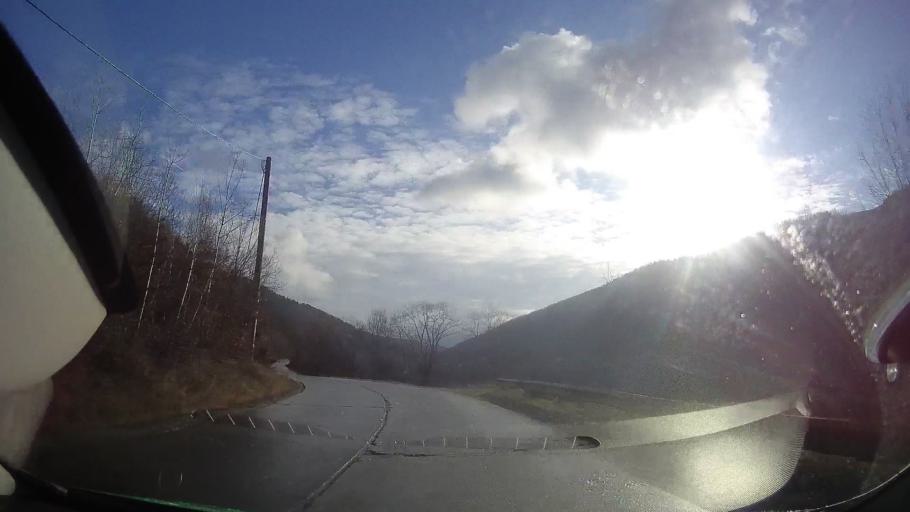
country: RO
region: Alba
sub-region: Comuna Sohodol
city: Sohodol
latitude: 46.3810
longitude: 23.0036
